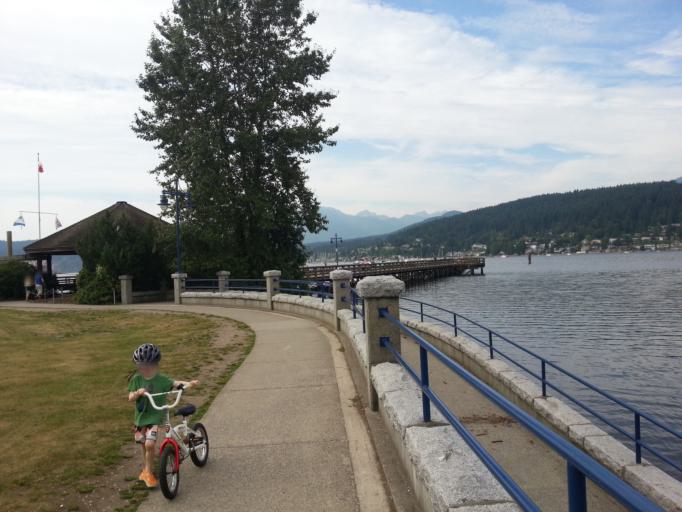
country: CA
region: British Columbia
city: Port Moody
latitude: 49.2814
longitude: -122.8494
